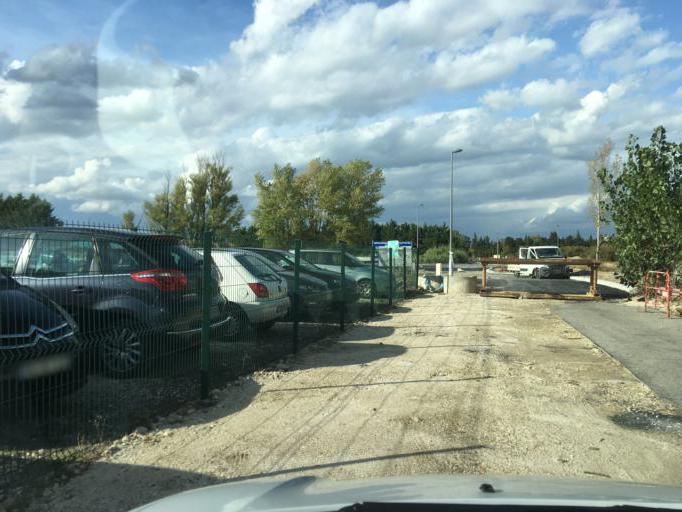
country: FR
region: Provence-Alpes-Cote d'Azur
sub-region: Departement du Vaucluse
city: Le Thor
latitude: 43.9236
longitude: 5.0158
